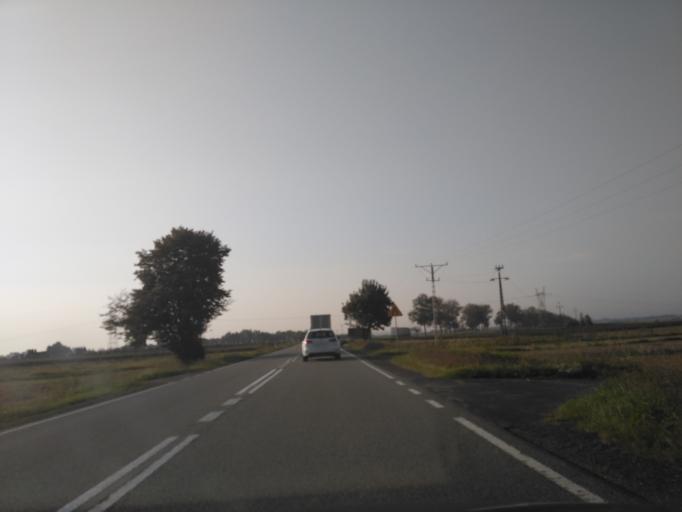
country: PL
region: Lublin Voivodeship
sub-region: Powiat krasnicki
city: Szastarka
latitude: 50.8177
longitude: 22.3177
